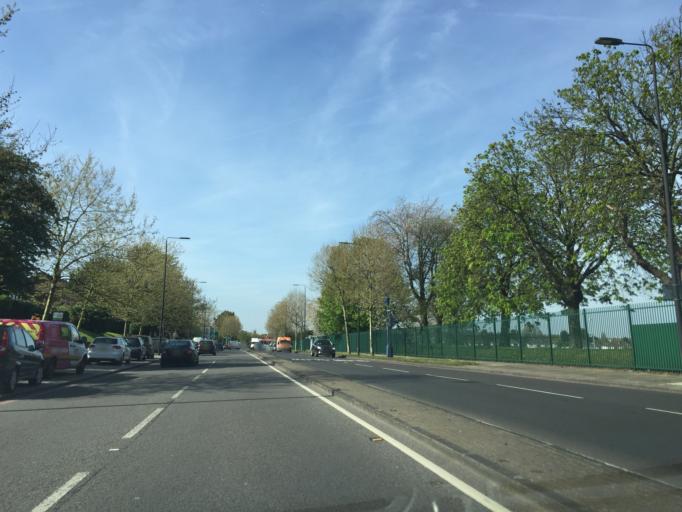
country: GB
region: England
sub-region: Greater London
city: Blackheath
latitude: 51.4469
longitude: 0.0306
